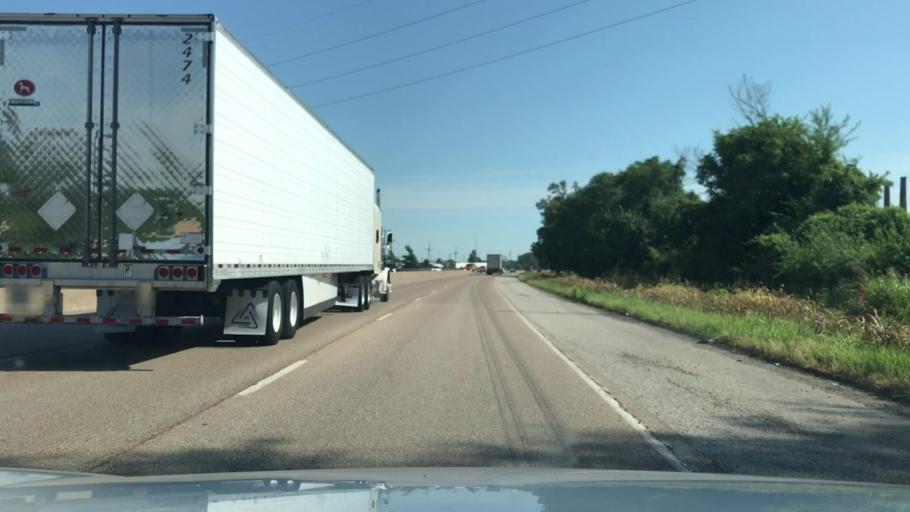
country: US
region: Illinois
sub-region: Madison County
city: Venice
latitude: 38.6850
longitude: -90.1723
